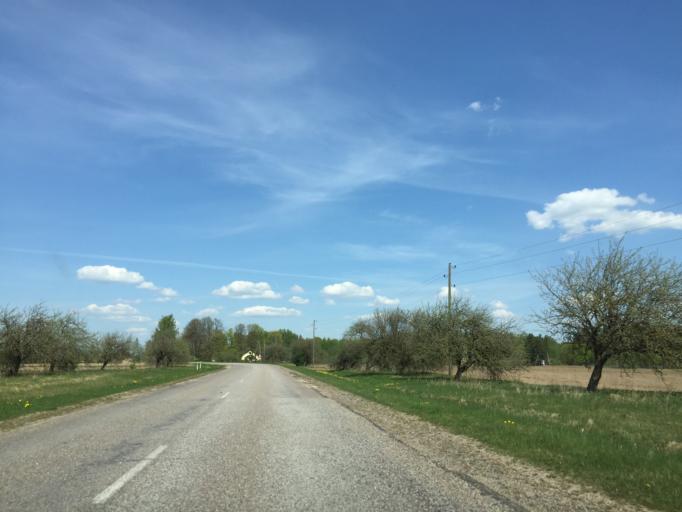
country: LV
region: Krimulda
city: Ragana
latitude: 57.3196
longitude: 24.6418
